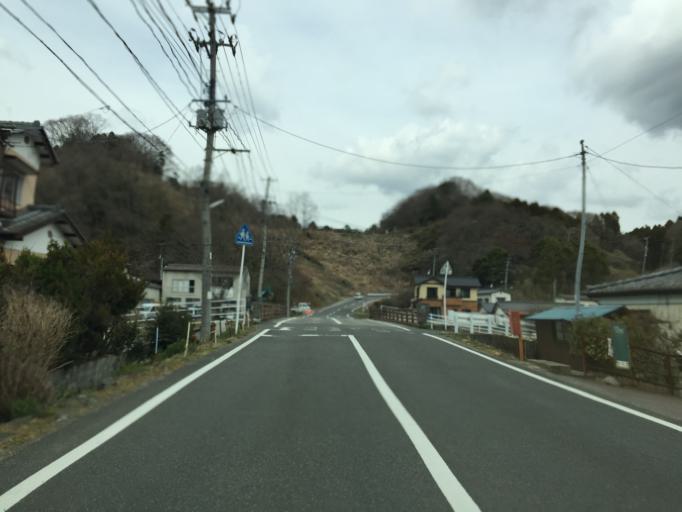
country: JP
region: Fukushima
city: Iwaki
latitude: 37.0324
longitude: 140.8426
